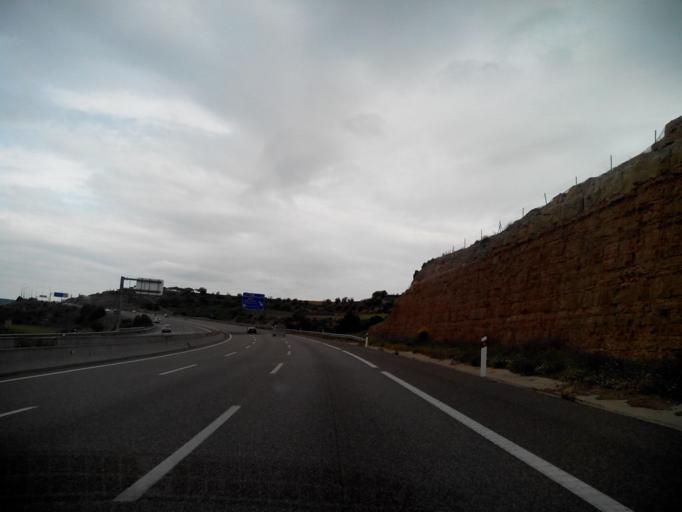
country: ES
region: Catalonia
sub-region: Provincia de Lleida
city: Cervera
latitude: 41.6875
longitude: 1.2633
